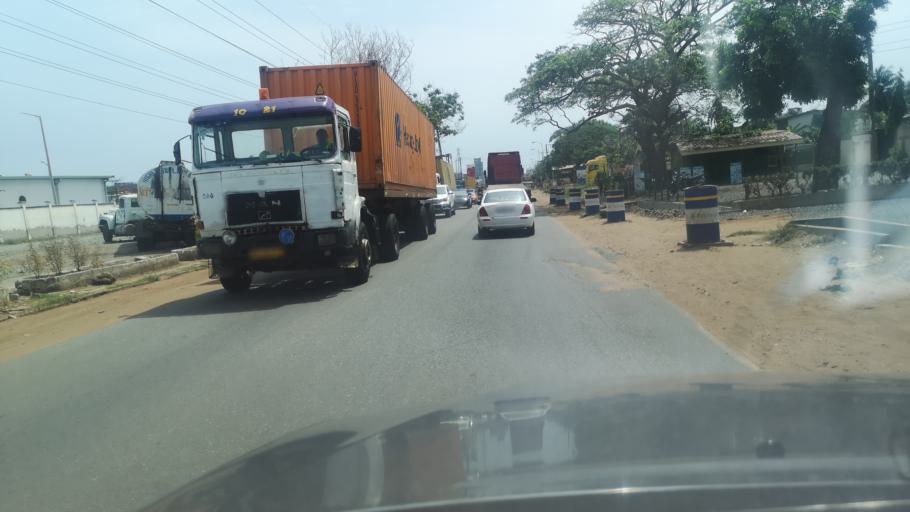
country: GH
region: Greater Accra
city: Tema
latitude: 5.6306
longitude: -0.0068
